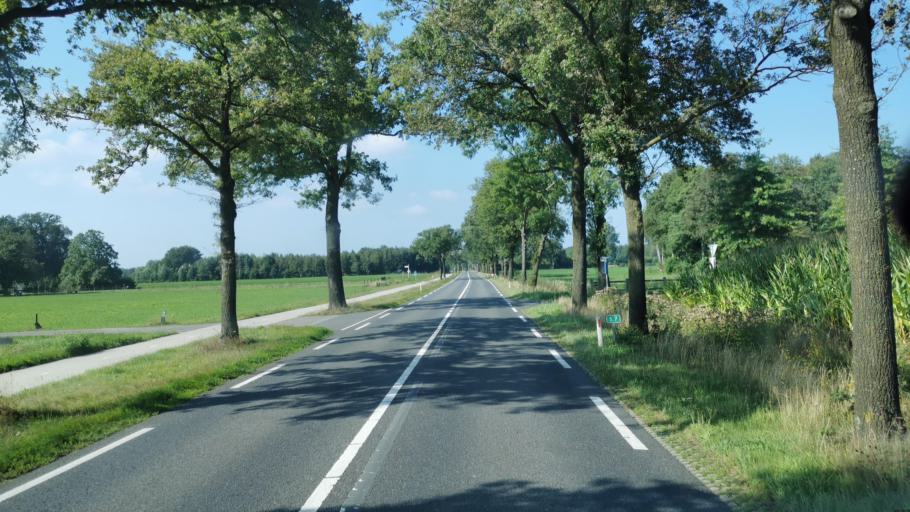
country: NL
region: Overijssel
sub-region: Gemeente Oldenzaal
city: Oldenzaal
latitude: 52.3667
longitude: 6.9118
